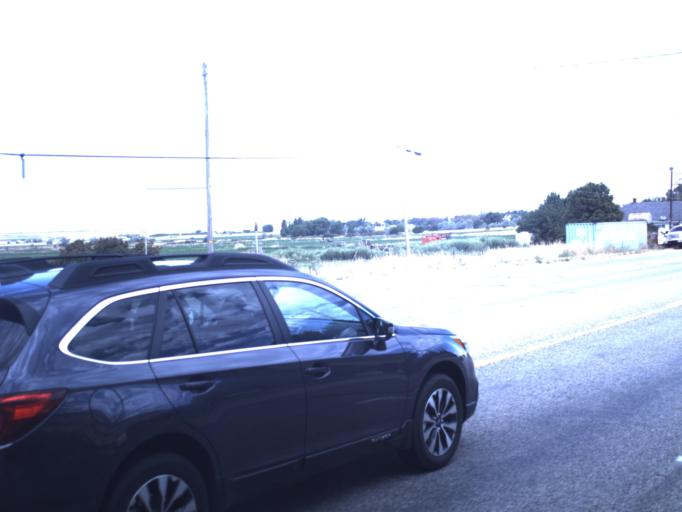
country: US
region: Utah
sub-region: Box Elder County
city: Willard
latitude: 41.4328
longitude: -112.0355
